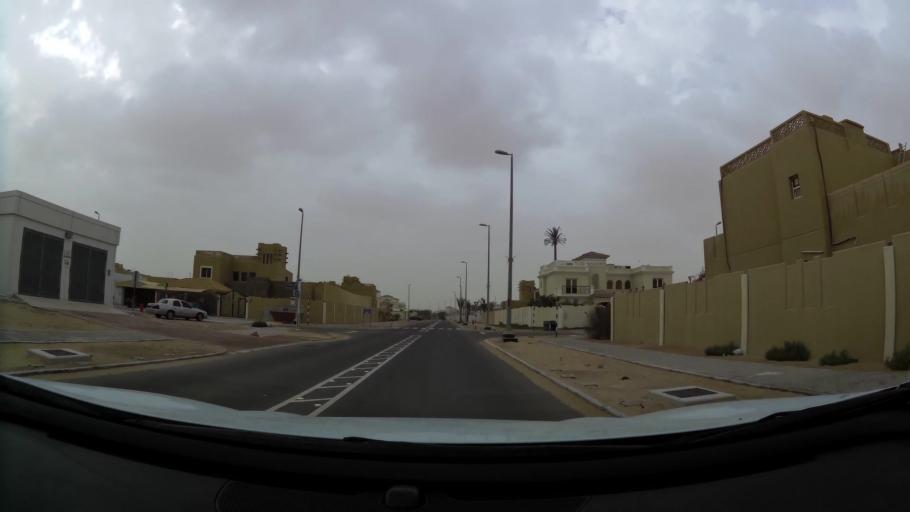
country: AE
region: Abu Dhabi
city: Abu Dhabi
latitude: 24.4434
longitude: 54.7127
